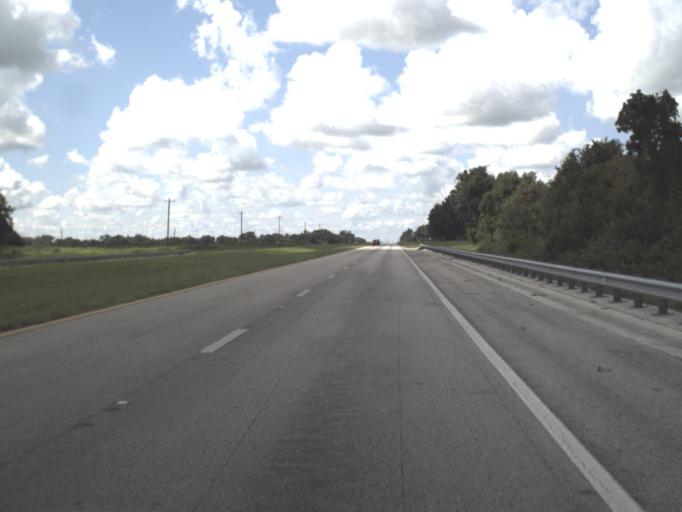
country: US
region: Florida
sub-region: DeSoto County
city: Arcadia
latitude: 27.3073
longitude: -81.8200
